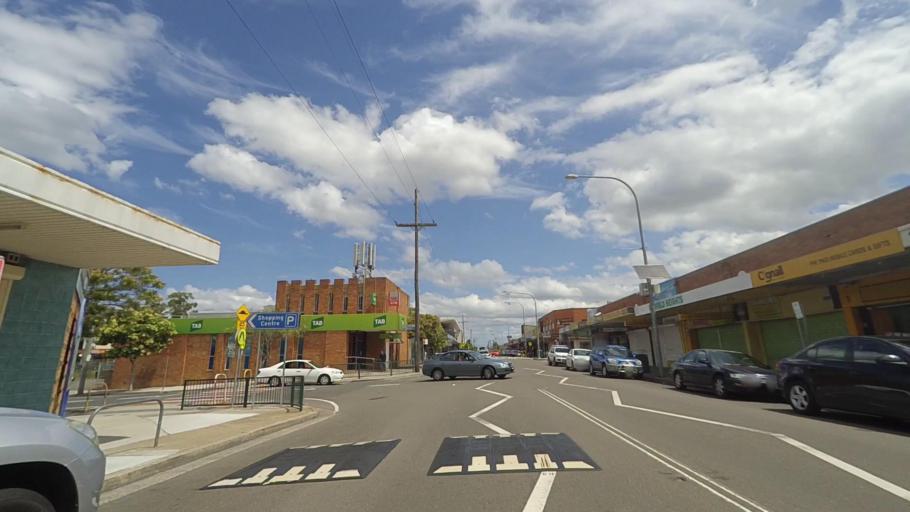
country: AU
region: New South Wales
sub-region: Fairfield
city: Fairfield Heights
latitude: -33.8633
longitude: 150.9387
